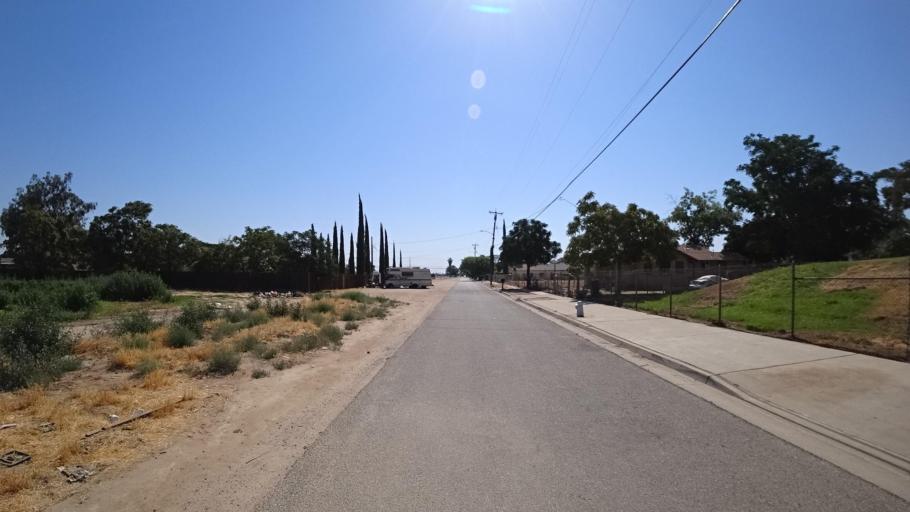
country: US
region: California
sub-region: Fresno County
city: West Park
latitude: 36.7105
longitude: -119.8114
